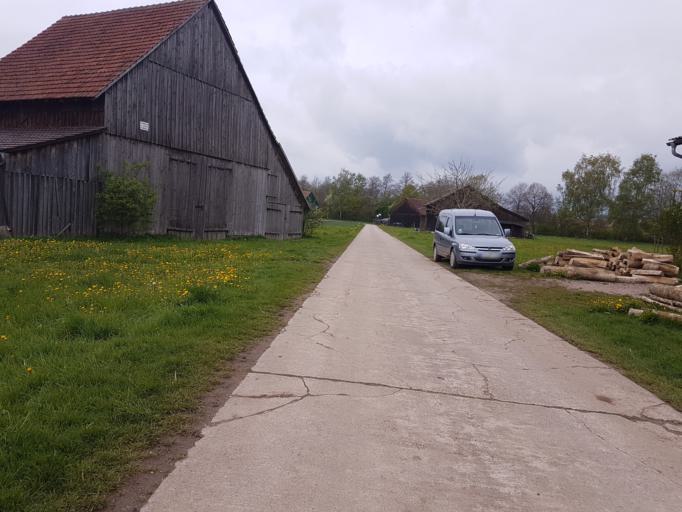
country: DE
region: Baden-Wuerttemberg
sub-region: Freiburg Region
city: Hufingen
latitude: 47.9307
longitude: 8.5002
